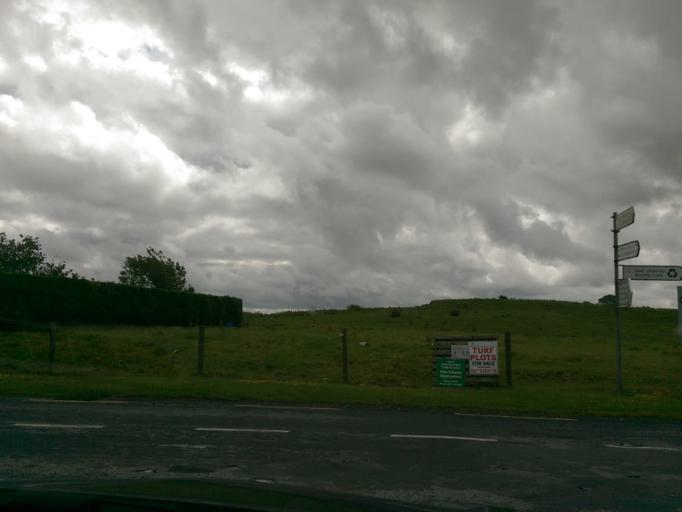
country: IE
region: Connaught
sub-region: County Galway
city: Loughrea
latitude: 53.3206
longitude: -8.4635
